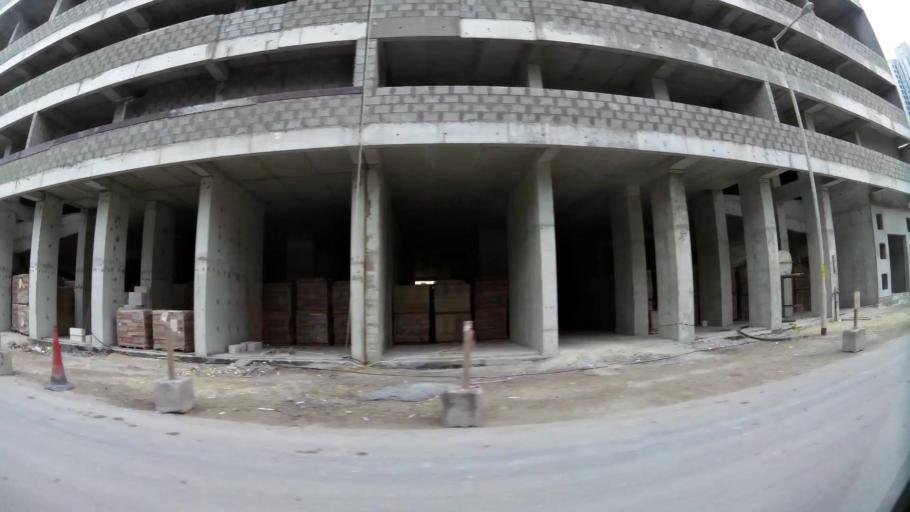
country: BH
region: Muharraq
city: Al Muharraq
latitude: 26.2391
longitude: 50.5944
